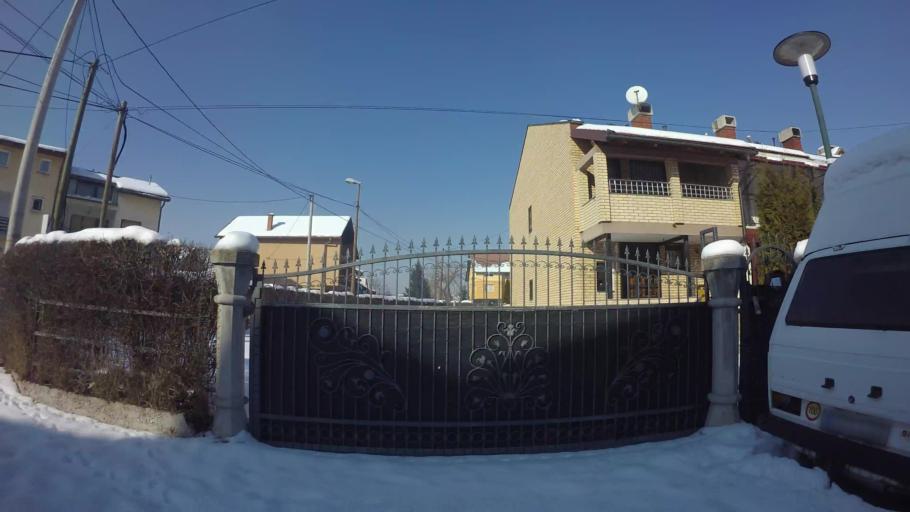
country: BA
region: Federation of Bosnia and Herzegovina
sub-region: Kanton Sarajevo
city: Sarajevo
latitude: 43.8143
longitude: 18.3176
